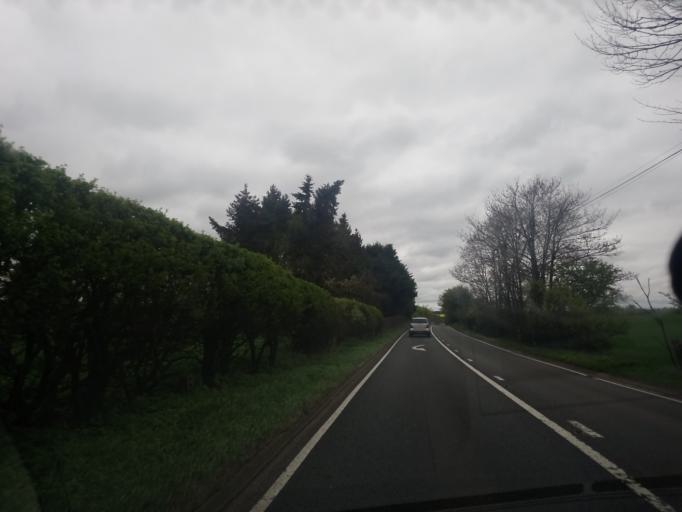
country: GB
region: England
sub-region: Telford and Wrekin
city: Chetwynd
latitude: 52.8065
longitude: -2.4349
